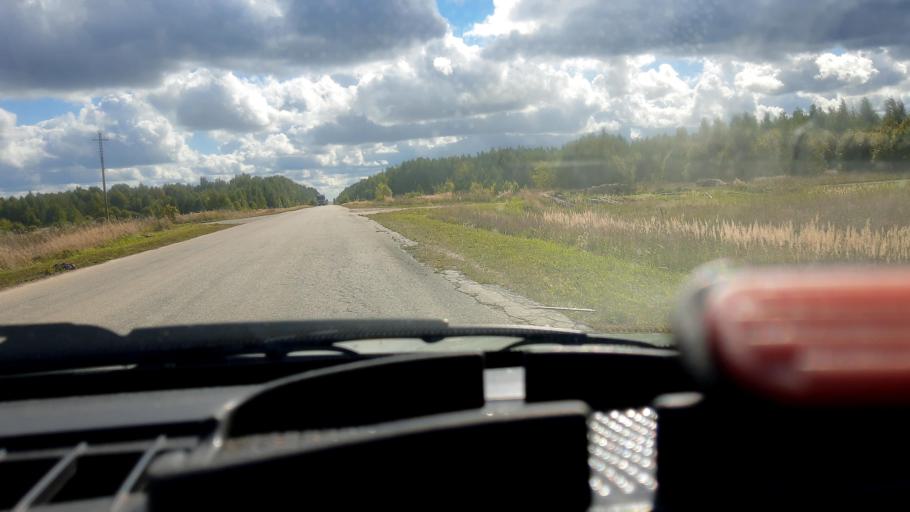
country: RU
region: Mariy-El
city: Kilemary
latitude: 56.9334
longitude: 46.6983
